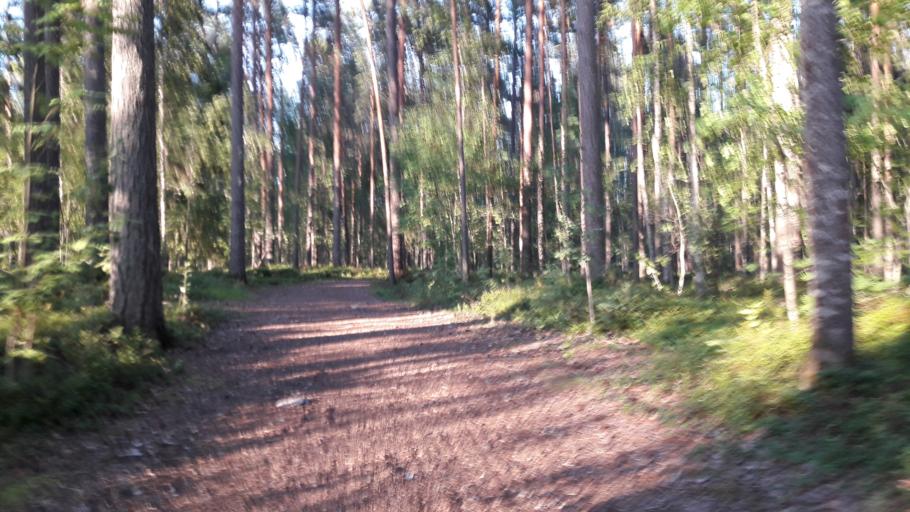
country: FI
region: North Karelia
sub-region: Joensuu
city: Joensuu
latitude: 62.6147
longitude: 29.7169
